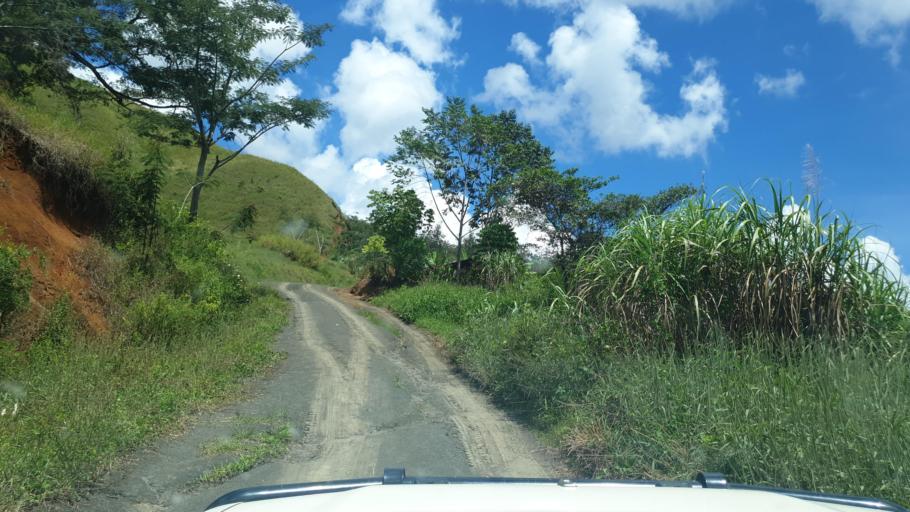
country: PG
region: Chimbu
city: Kundiawa
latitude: -6.2560
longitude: 145.1380
